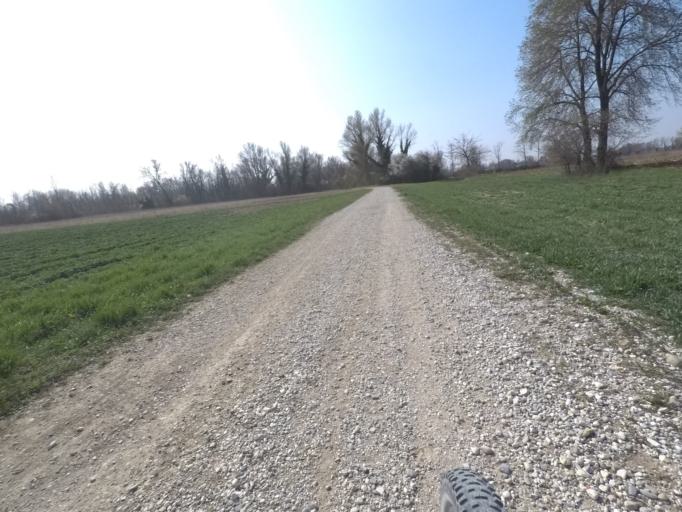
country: IT
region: Friuli Venezia Giulia
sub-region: Provincia di Udine
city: Remanzacco
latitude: 46.0653
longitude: 13.3291
